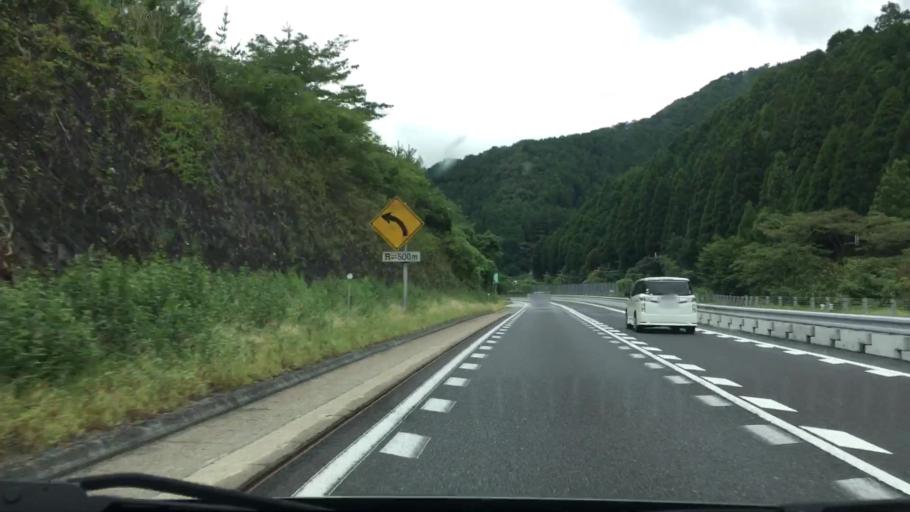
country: JP
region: Hyogo
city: Yamazakicho-nakabirose
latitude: 35.0456
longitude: 134.4620
